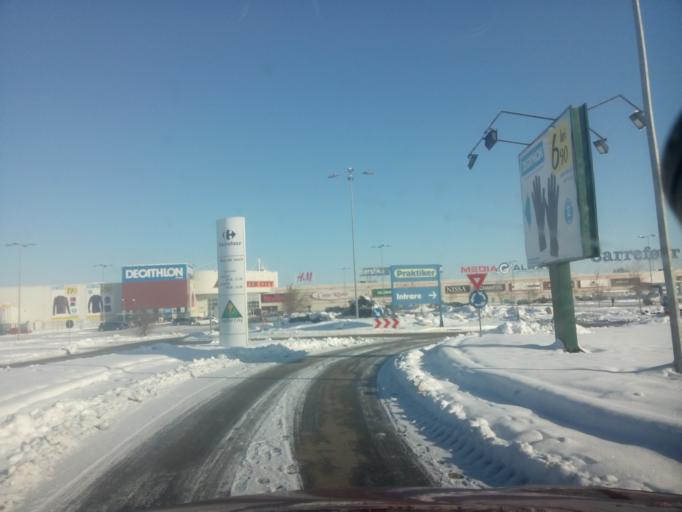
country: RO
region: Arges
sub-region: Oras Stefanesti
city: Golesti
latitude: 44.8176
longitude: 24.9398
